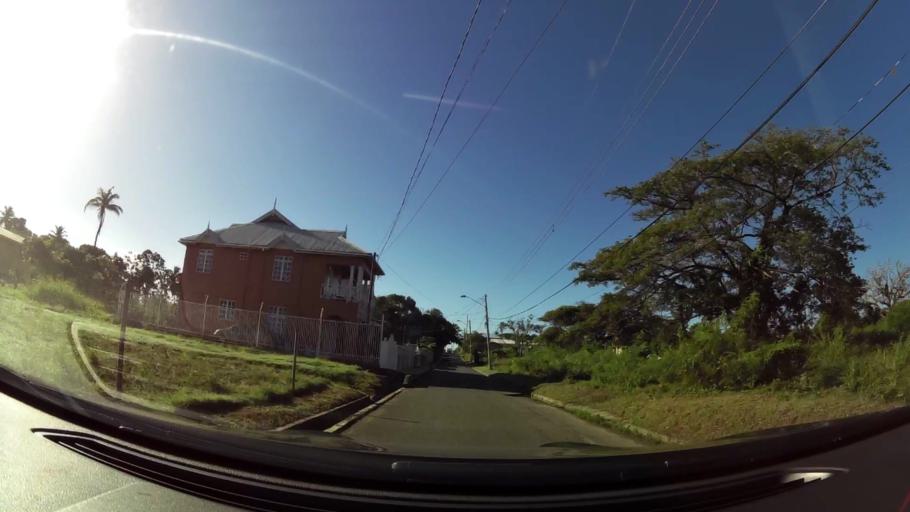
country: TT
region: Tobago
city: Scarborough
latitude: 11.1544
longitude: -60.8207
